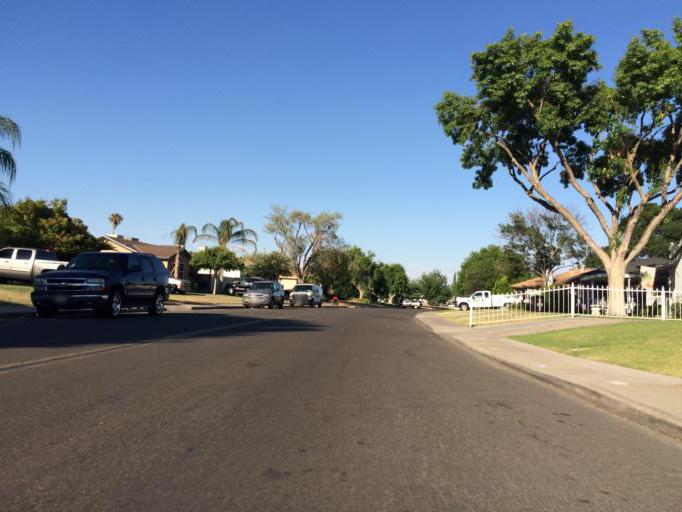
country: US
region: California
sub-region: Fresno County
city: Fresno
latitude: 36.7689
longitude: -119.7695
